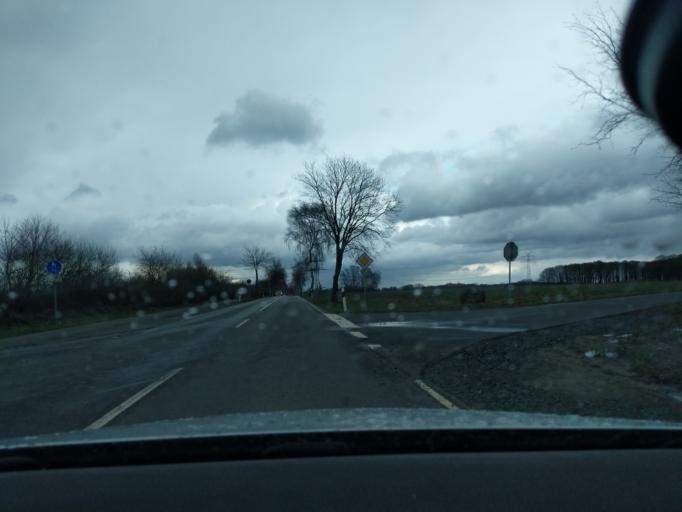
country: DE
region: Lower Saxony
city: Kutenholz
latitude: 53.5065
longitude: 9.3592
